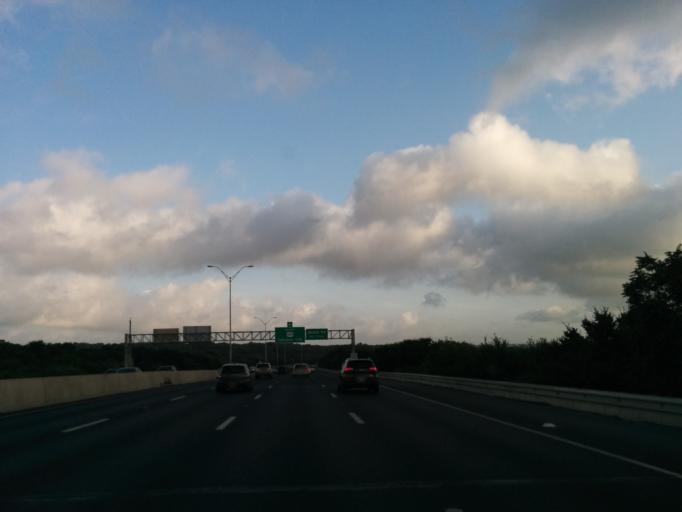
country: US
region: Texas
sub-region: Bexar County
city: Olmos Park
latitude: 29.4718
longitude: -98.4773
